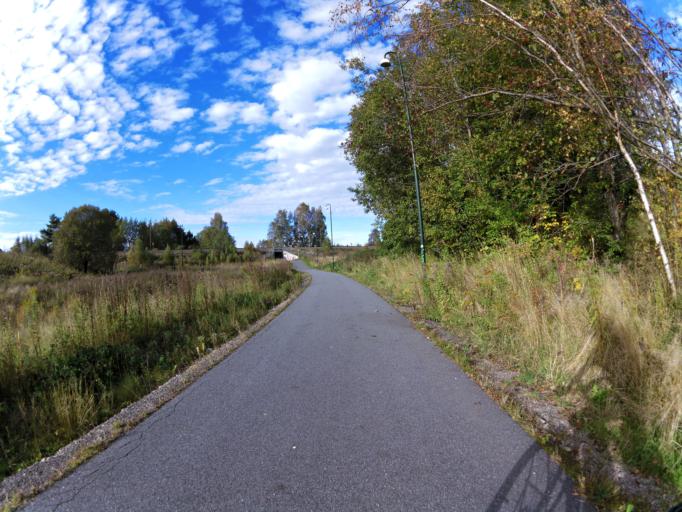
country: NO
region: Ostfold
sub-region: Sarpsborg
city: Sarpsborg
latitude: 59.2849
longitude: 11.0949
